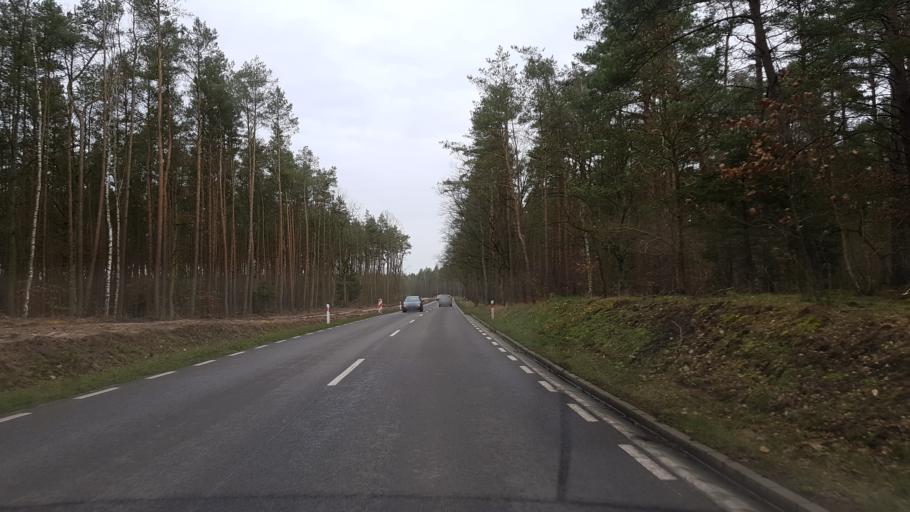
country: PL
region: West Pomeranian Voivodeship
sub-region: Powiat policki
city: Police
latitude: 53.6335
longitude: 14.5037
